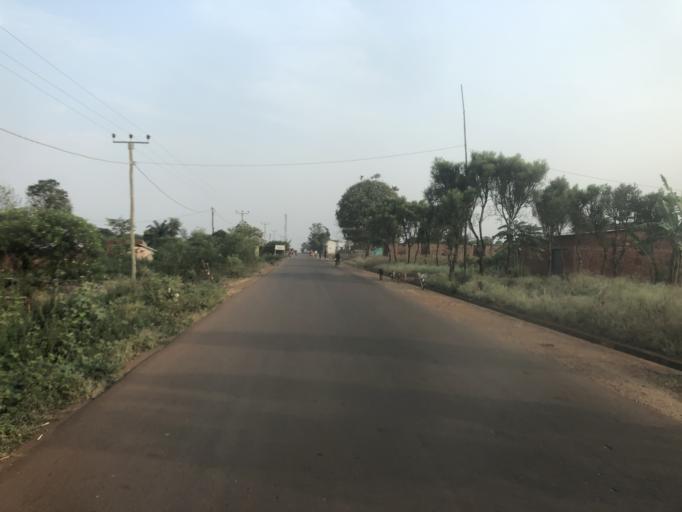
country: BI
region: Cibitoke
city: Cibitoke
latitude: -2.7249
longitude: 29.0042
